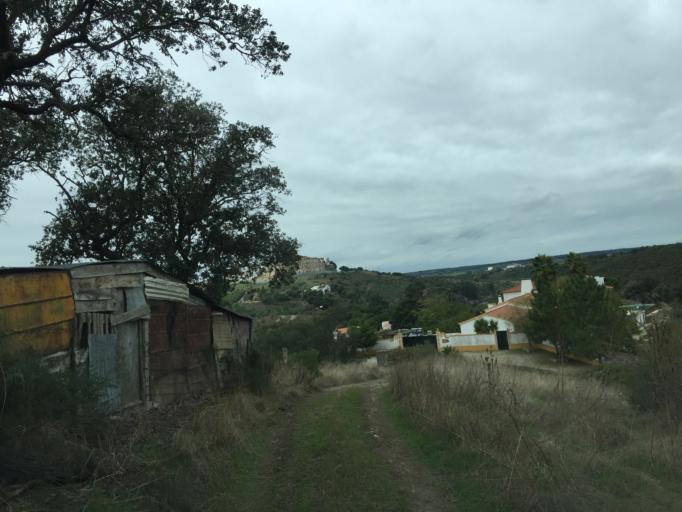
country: PT
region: Portalegre
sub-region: Avis
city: Avis
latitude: 39.0531
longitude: -7.8809
